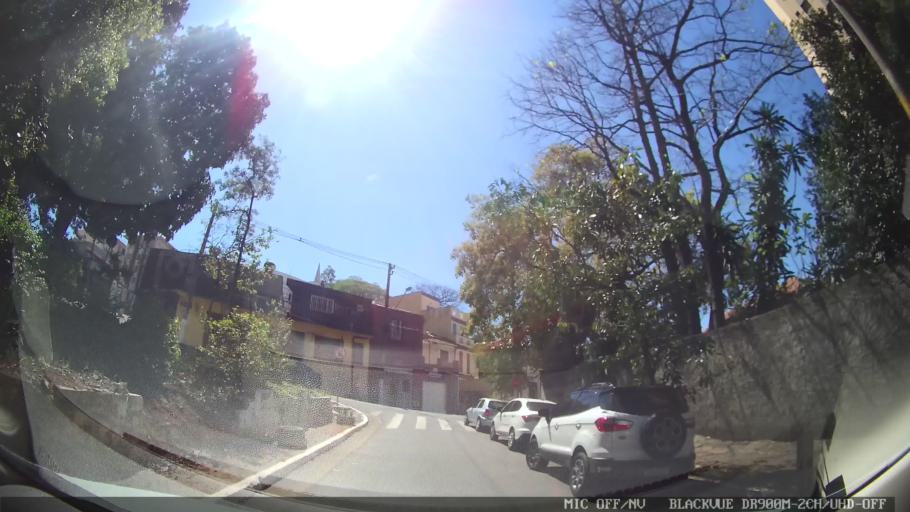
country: BR
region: Sao Paulo
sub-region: Sao Paulo
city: Sao Paulo
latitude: -23.5077
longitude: -46.6613
